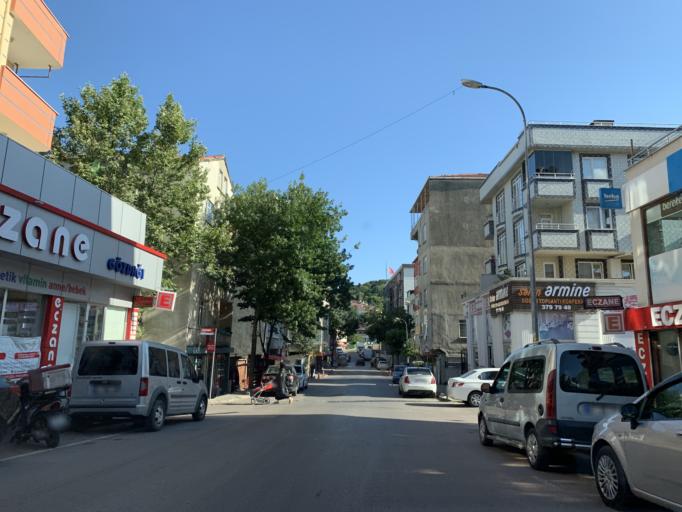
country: TR
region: Istanbul
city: Pendik
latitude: 40.8956
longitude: 29.2543
